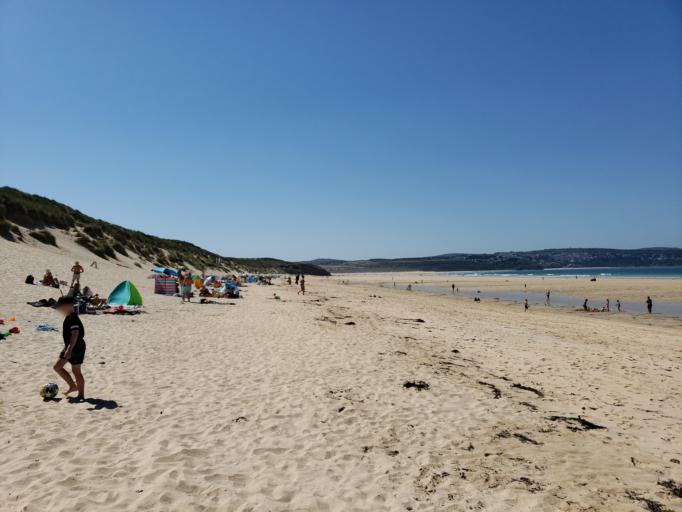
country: GB
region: England
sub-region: Cornwall
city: Hayle
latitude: 50.2061
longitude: -5.4145
